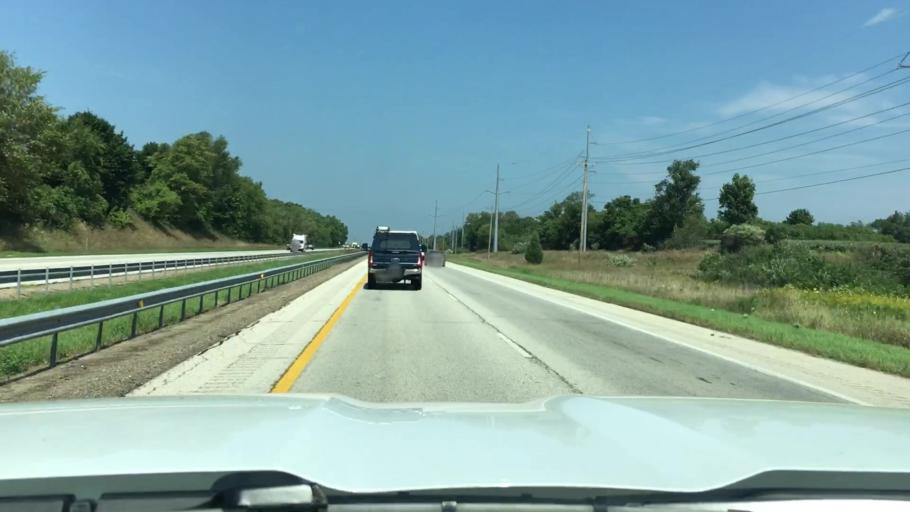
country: US
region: Michigan
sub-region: Kalamazoo County
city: Schoolcraft
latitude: 42.0578
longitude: -85.6359
